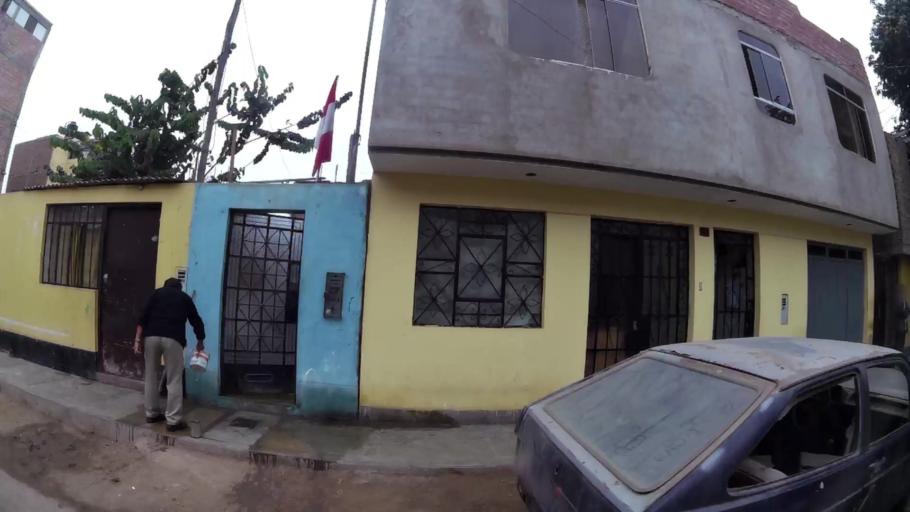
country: PE
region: Lima
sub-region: Lima
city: Surco
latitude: -12.1536
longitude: -77.0152
